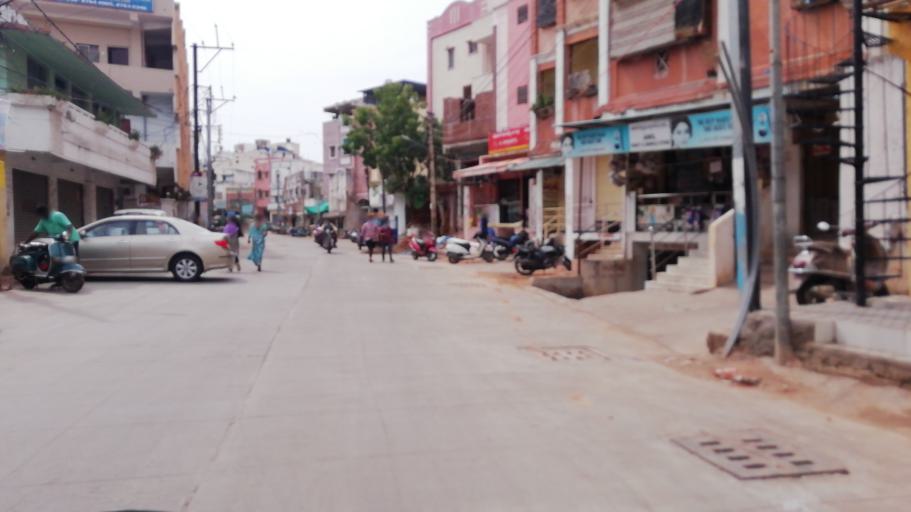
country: IN
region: Telangana
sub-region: Hyderabad
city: Malkajgiri
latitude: 17.4135
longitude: 78.5053
